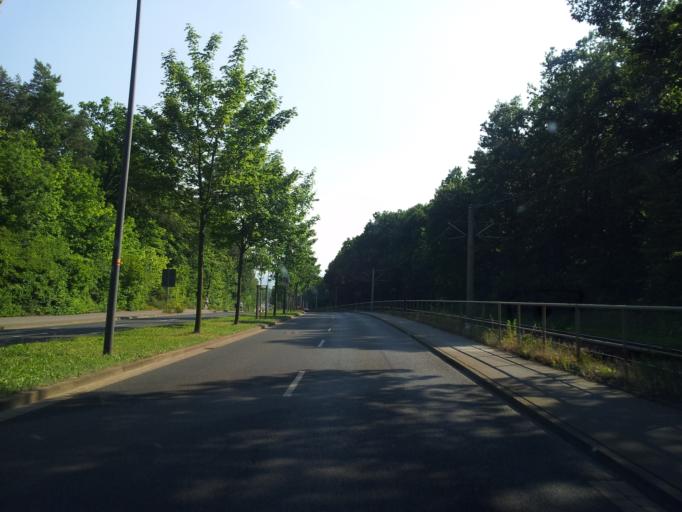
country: DE
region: Saxony
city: Albertstadt
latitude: 51.1066
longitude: 13.7721
